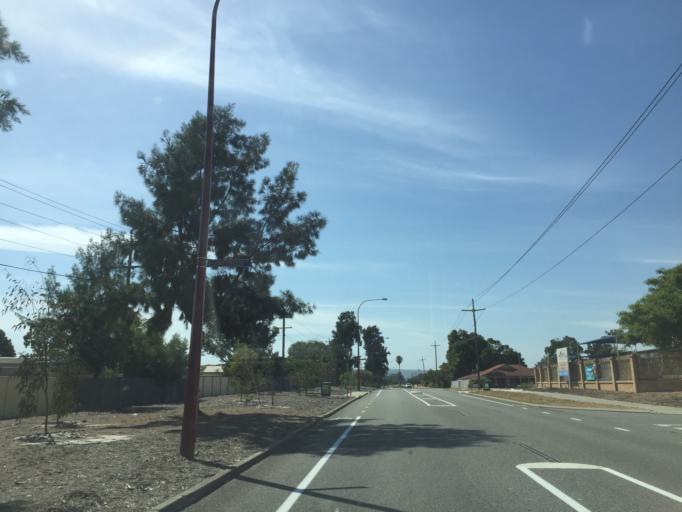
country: AU
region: Western Australia
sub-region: Gosnells
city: Thornlie
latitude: -32.0765
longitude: 115.9628
